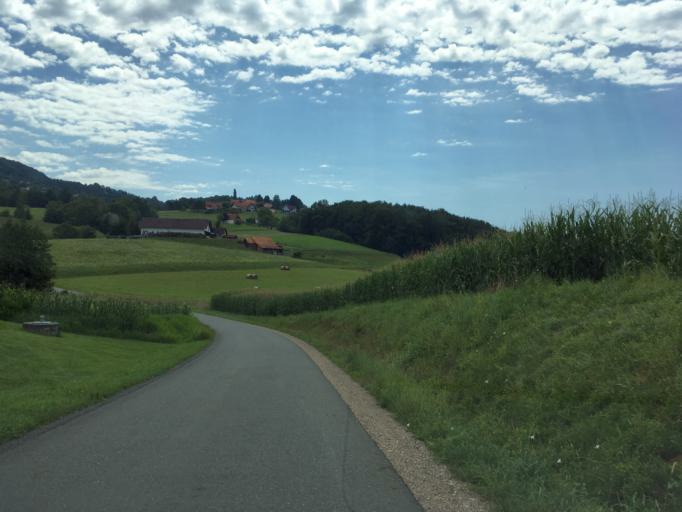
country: AT
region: Styria
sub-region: Politischer Bezirk Deutschlandsberg
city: Wettmannstatten
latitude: 46.7921
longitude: 15.3986
